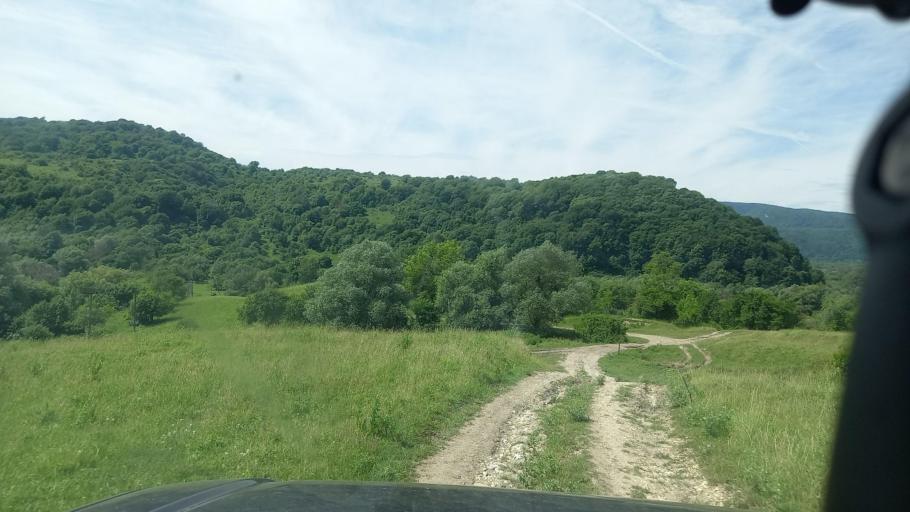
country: RU
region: Karachayevo-Cherkesiya
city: Kurdzhinovo
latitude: 44.1441
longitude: 41.0575
